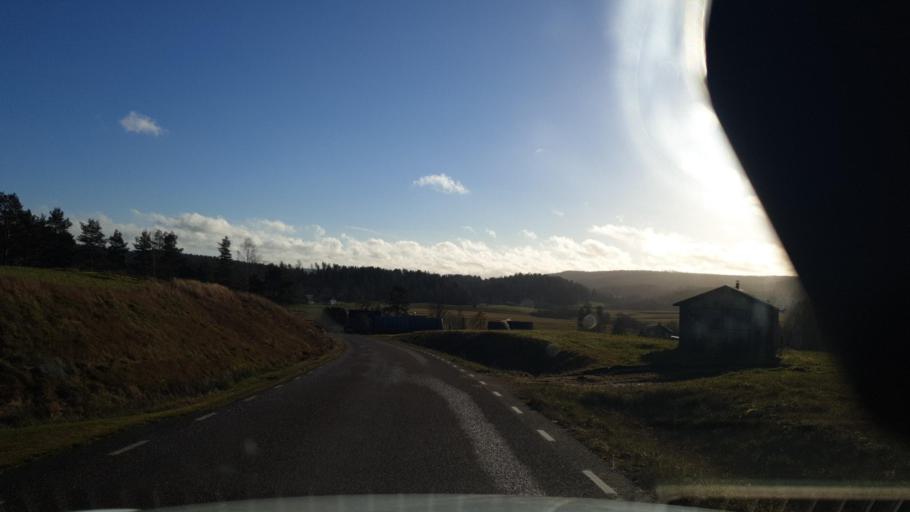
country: NO
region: Ostfold
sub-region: Romskog
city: Romskog
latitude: 59.7122
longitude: 12.0703
